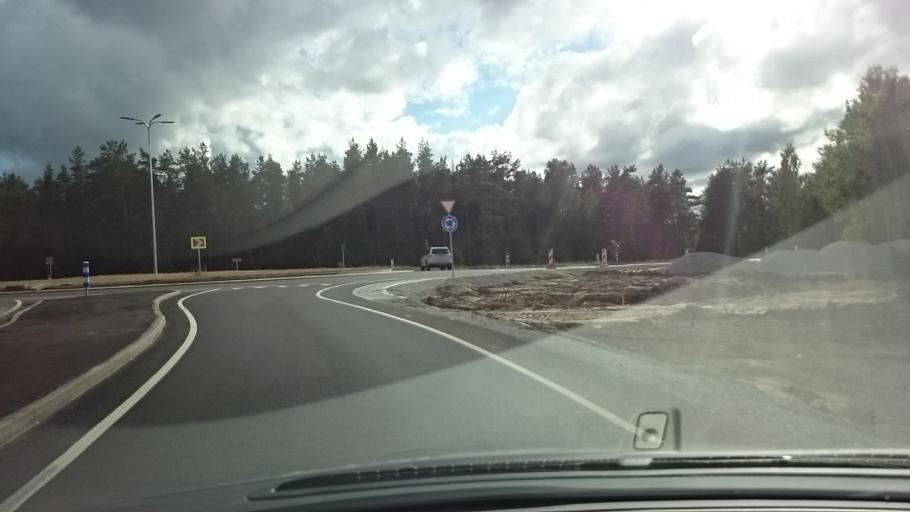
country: EE
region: Harju
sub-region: Saku vald
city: Saku
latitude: 59.3093
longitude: 24.6331
